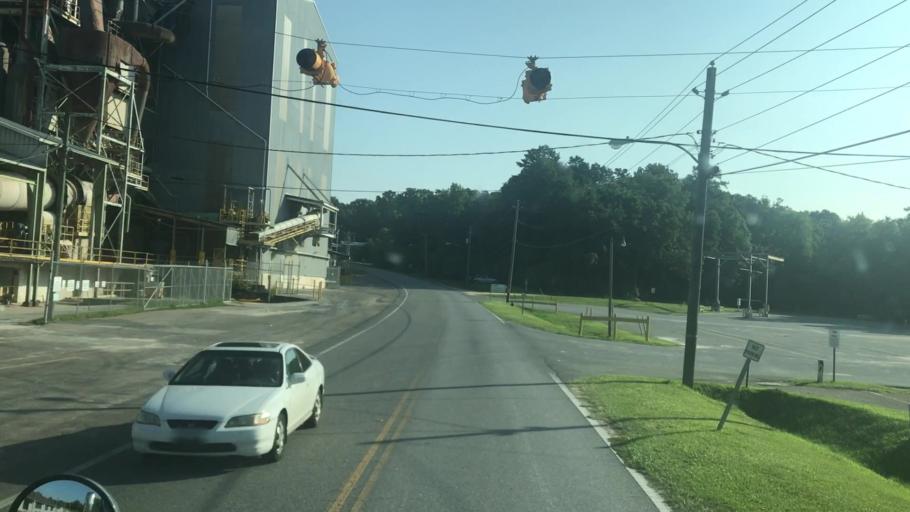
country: US
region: Florida
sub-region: Gadsden County
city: Quincy
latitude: 30.5997
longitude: -84.5732
